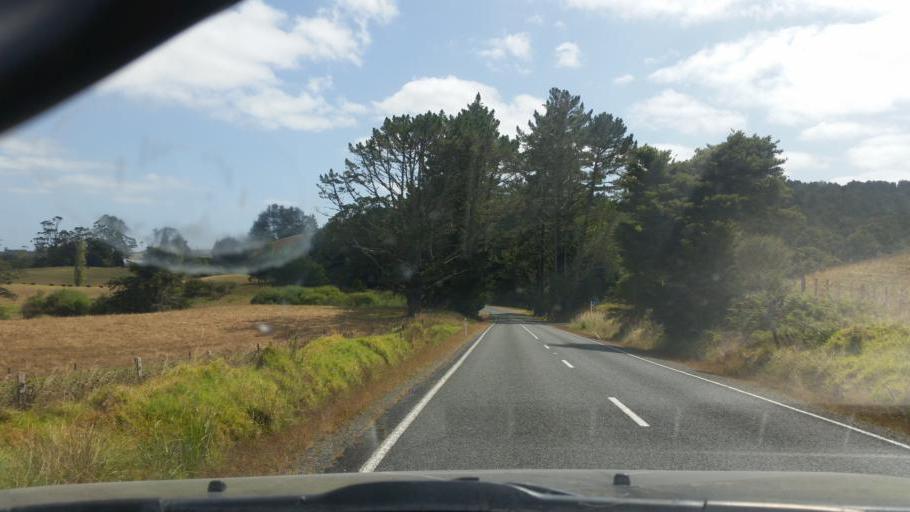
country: NZ
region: Northland
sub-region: Whangarei
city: Ruakaka
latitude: -35.9510
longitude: 174.2933
